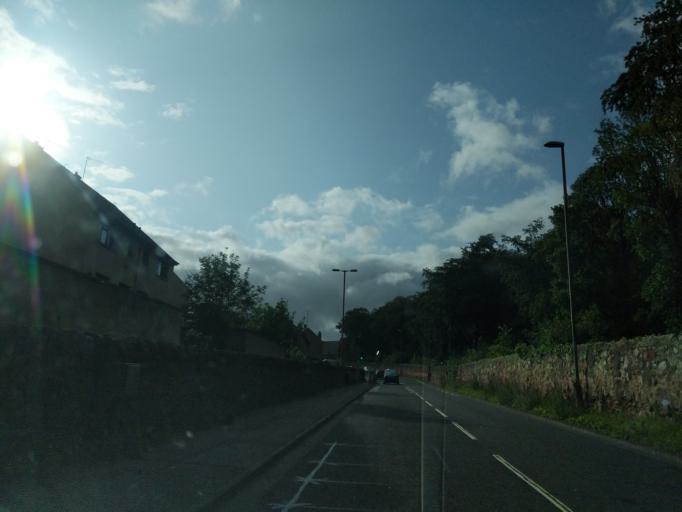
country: GB
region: Scotland
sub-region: Midlothian
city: Dalkeith
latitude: 55.8971
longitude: -3.0614
